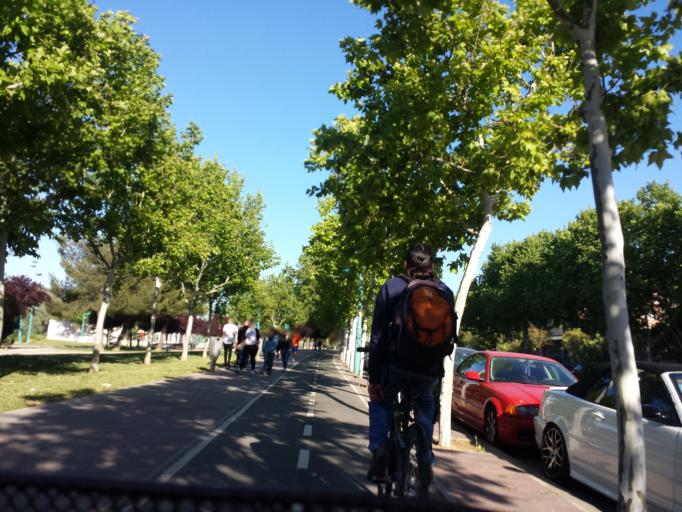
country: ES
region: Aragon
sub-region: Provincia de Zaragoza
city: Zaragoza
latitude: 41.6534
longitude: -0.8681
